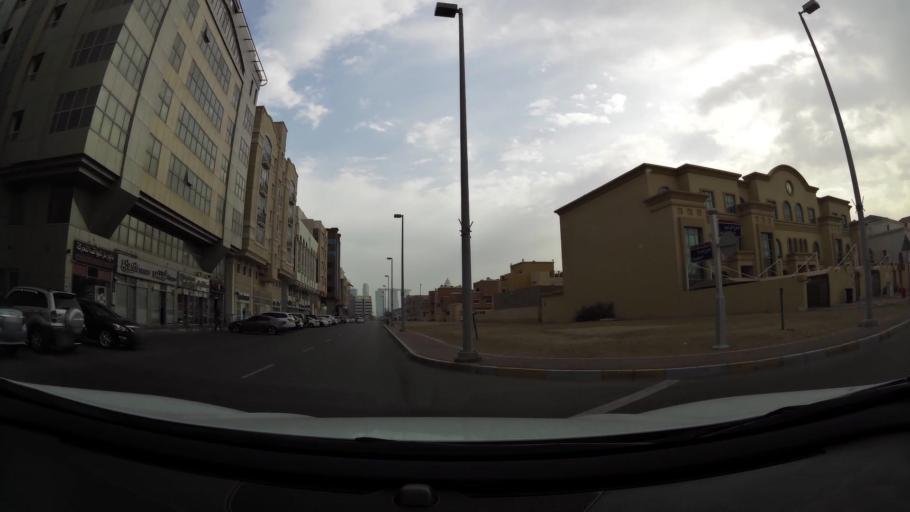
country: AE
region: Abu Dhabi
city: Abu Dhabi
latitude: 24.4748
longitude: 54.3797
